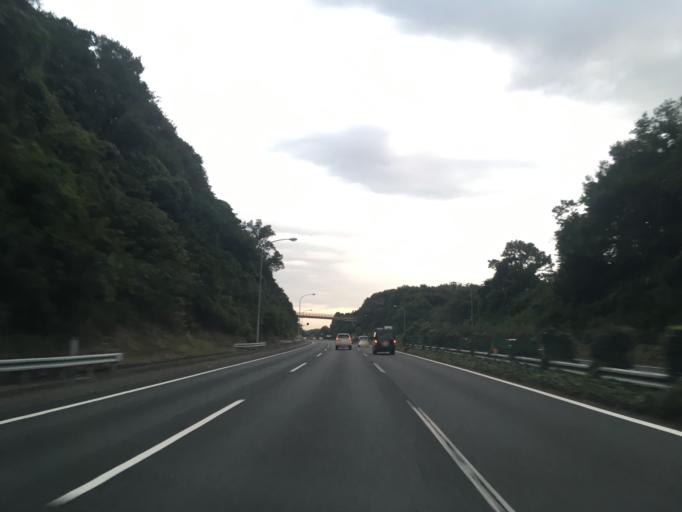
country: JP
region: Saitama
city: Ogawa
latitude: 36.0576
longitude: 139.3320
